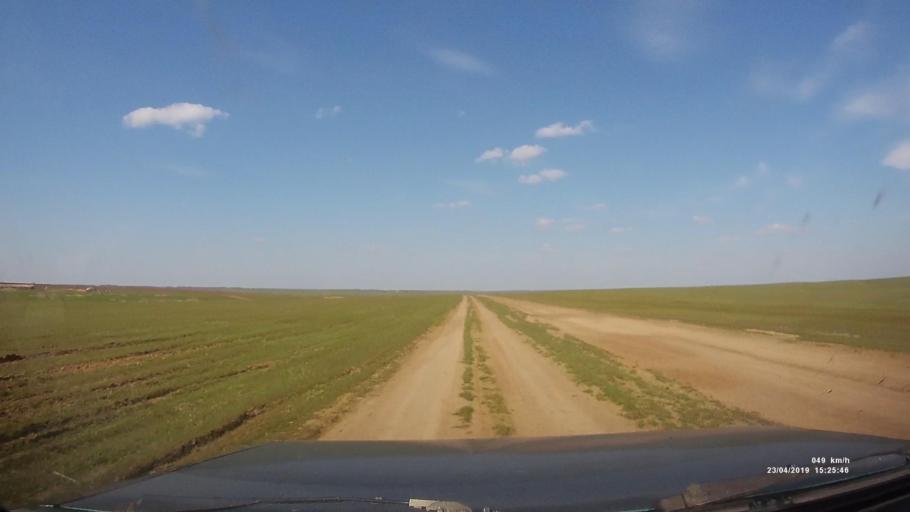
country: RU
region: Rostov
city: Remontnoye
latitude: 46.5429
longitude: 42.9841
